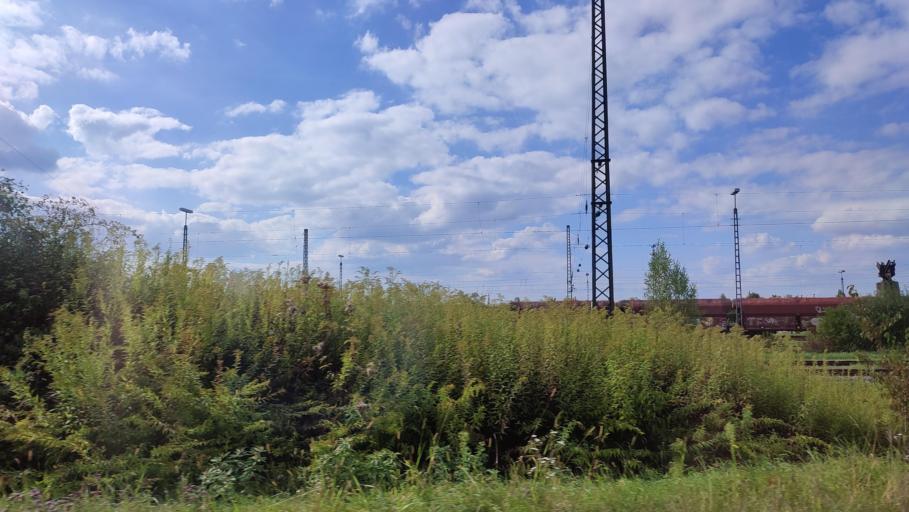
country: DE
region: Baden-Wuerttemberg
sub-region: Freiburg Region
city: Offenburg
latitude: 48.5004
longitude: 7.9609
